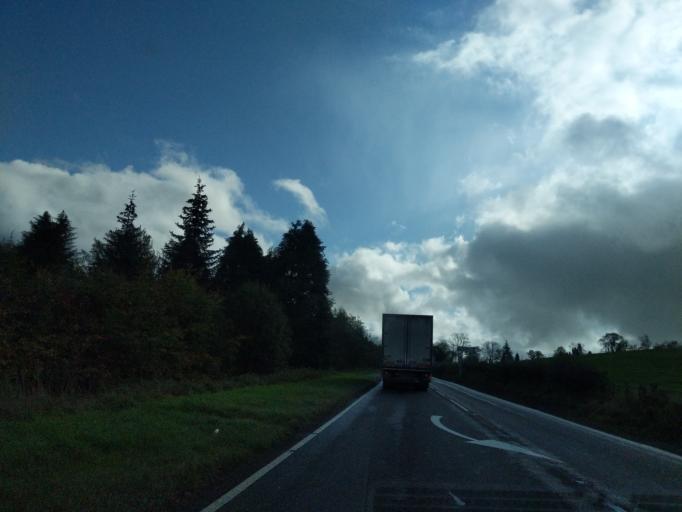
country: GB
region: Scotland
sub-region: Dumfries and Galloway
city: Moffat
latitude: 55.2853
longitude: -3.4450
